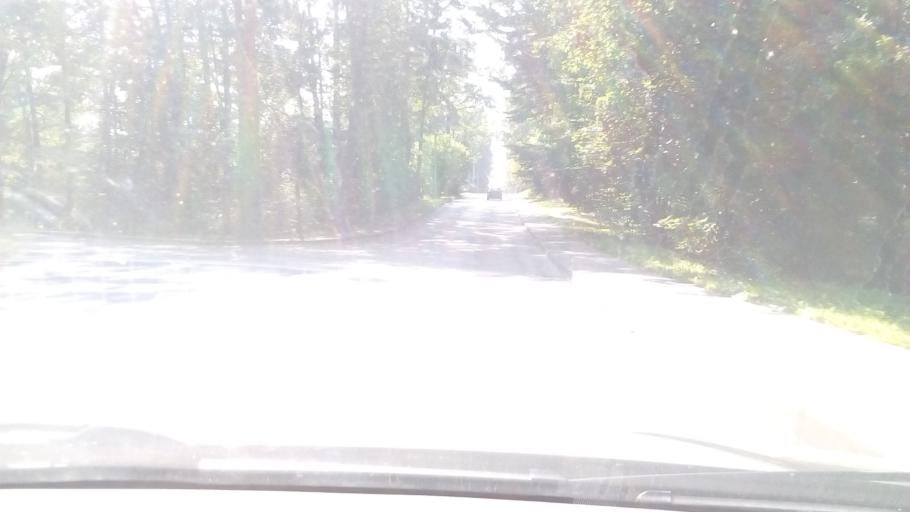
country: LT
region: Alytaus apskritis
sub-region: Alytus
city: Alytus
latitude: 54.3940
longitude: 24.0576
